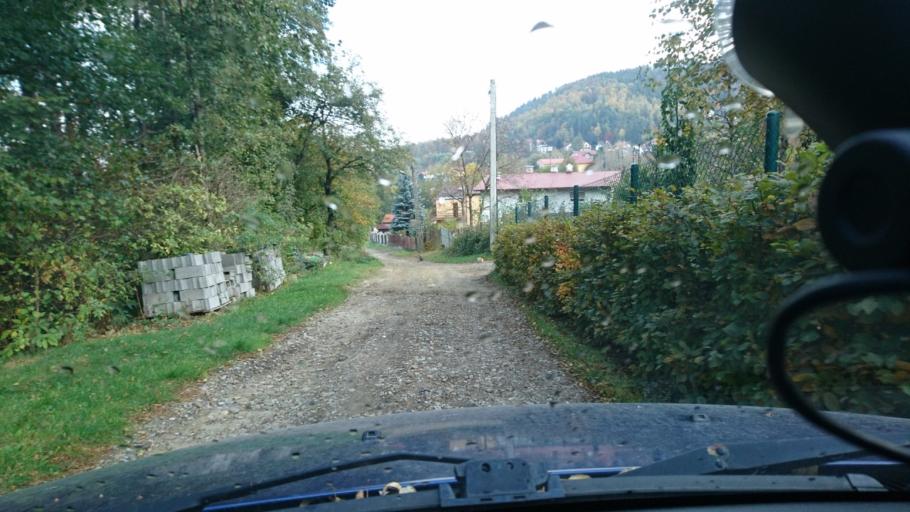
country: PL
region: Silesian Voivodeship
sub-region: Powiat bielski
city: Wilkowice
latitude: 49.7948
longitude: 19.0916
